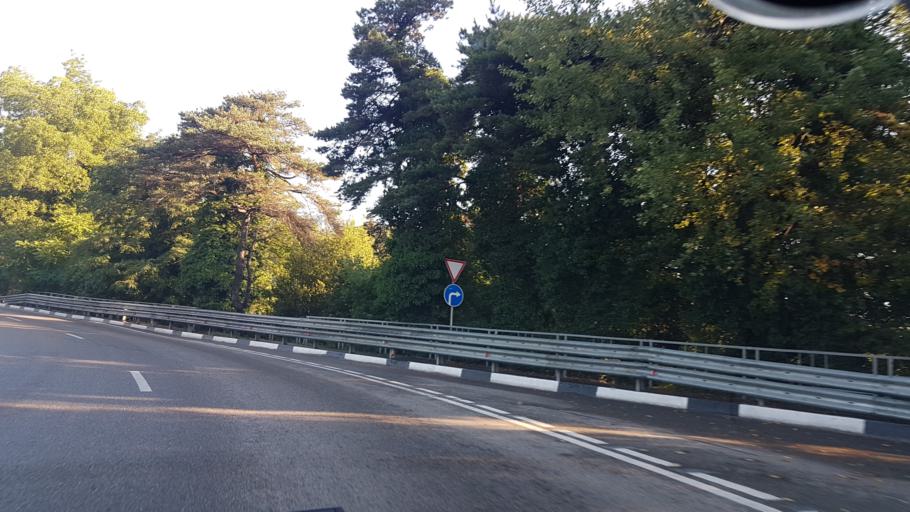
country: RU
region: Krasnodarskiy
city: Dagomys
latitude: 43.6436
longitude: 39.7018
